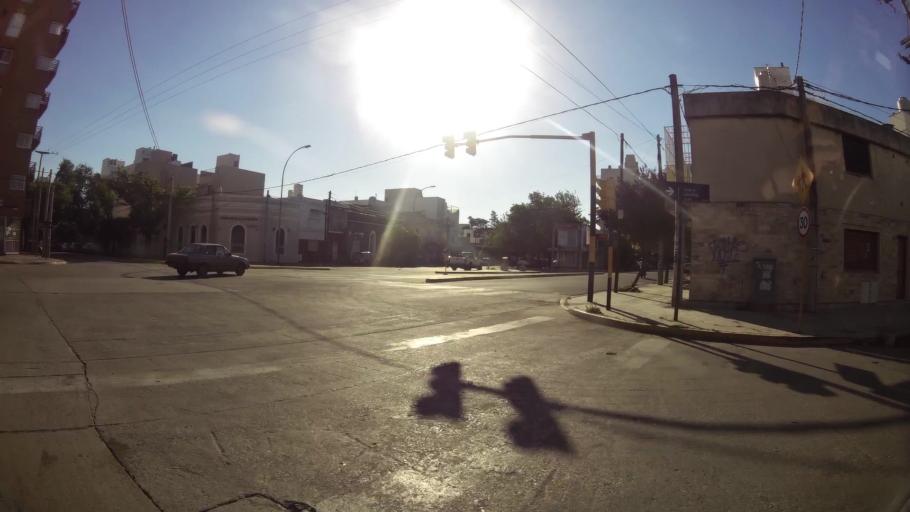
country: AR
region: Cordoba
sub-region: Departamento de Capital
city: Cordoba
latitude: -31.3915
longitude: -64.1825
